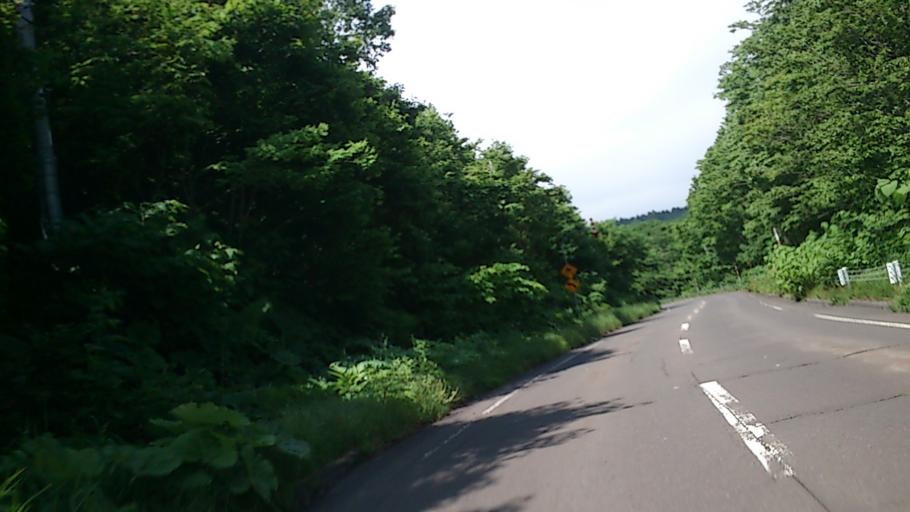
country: JP
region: Hokkaido
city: Niseko Town
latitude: 42.8235
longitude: 140.5298
